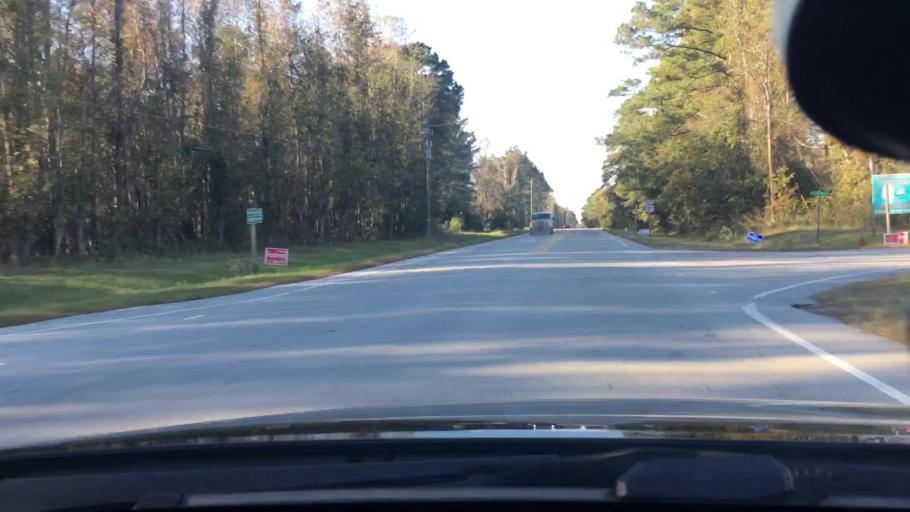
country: US
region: North Carolina
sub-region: Craven County
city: New Bern
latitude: 35.1951
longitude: -77.0542
